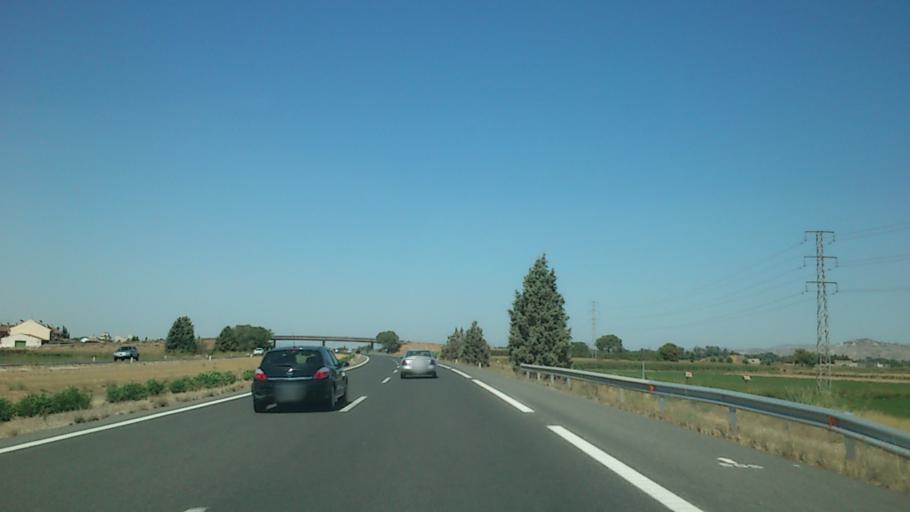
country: ES
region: Aragon
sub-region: Provincia de Zaragoza
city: Utebo
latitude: 41.7168
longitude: -0.9899
